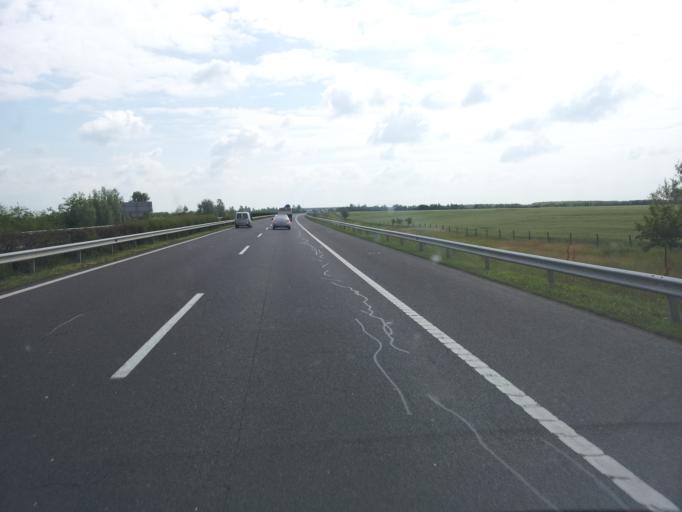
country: HU
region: Borsod-Abauj-Zemplen
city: Emod
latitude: 47.8841
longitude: 20.8492
